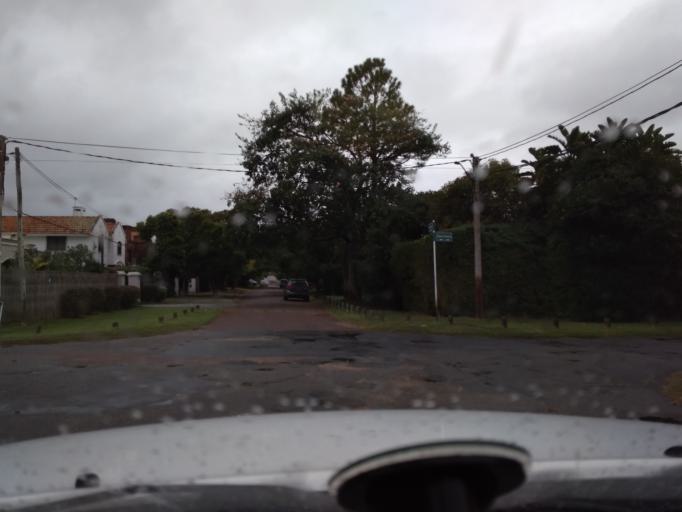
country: UY
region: Canelones
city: Barra de Carrasco
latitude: -34.8832
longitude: -56.0449
